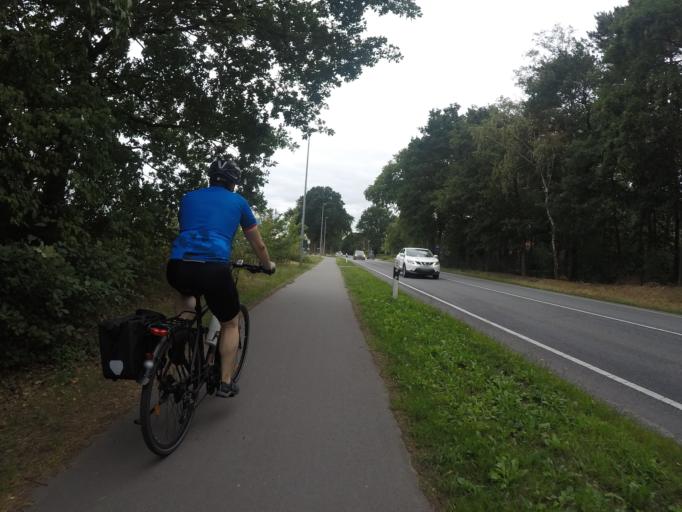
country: DE
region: Lower Saxony
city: Hemmoor
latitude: 53.6862
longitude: 9.1620
